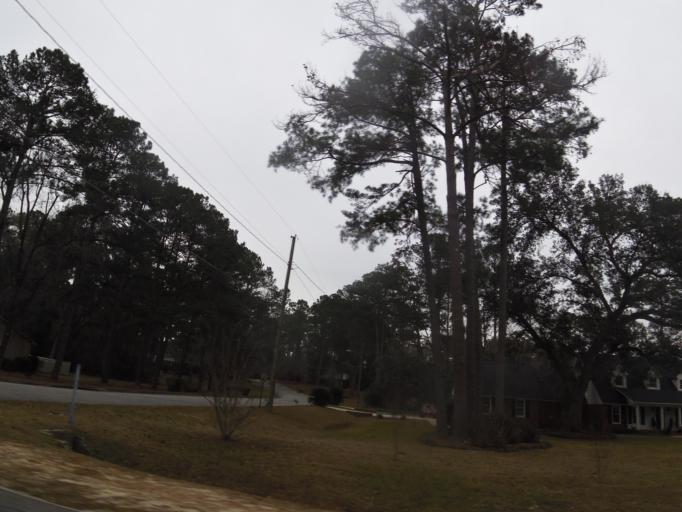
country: US
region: Georgia
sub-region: Thomas County
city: Thomasville
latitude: 30.8167
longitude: -83.9501
